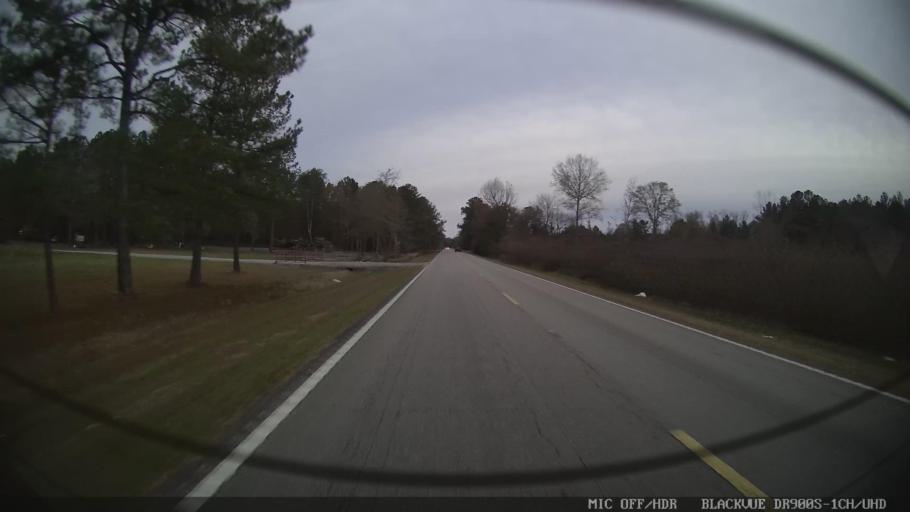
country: US
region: Mississippi
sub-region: Clarke County
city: Stonewall
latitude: 32.0346
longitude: -88.8731
